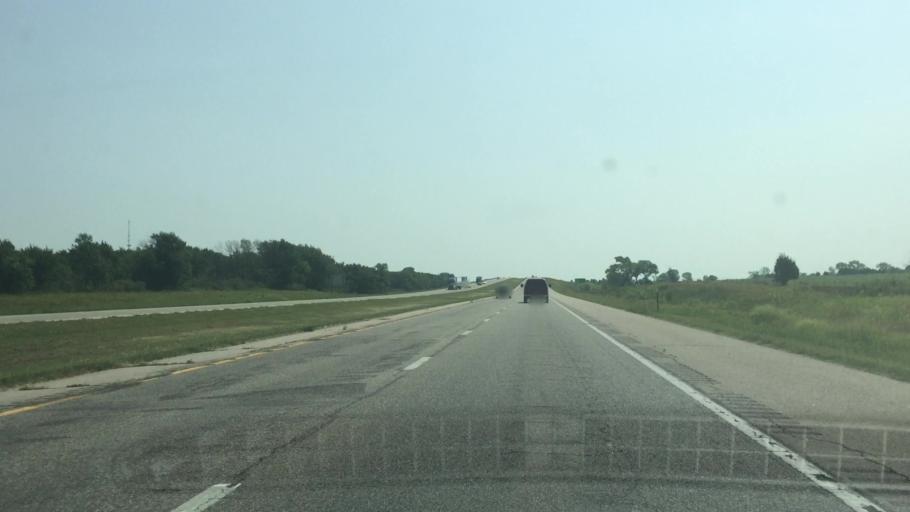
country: US
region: Kansas
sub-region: Osage County
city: Osage City
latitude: 38.4263
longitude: -95.8466
